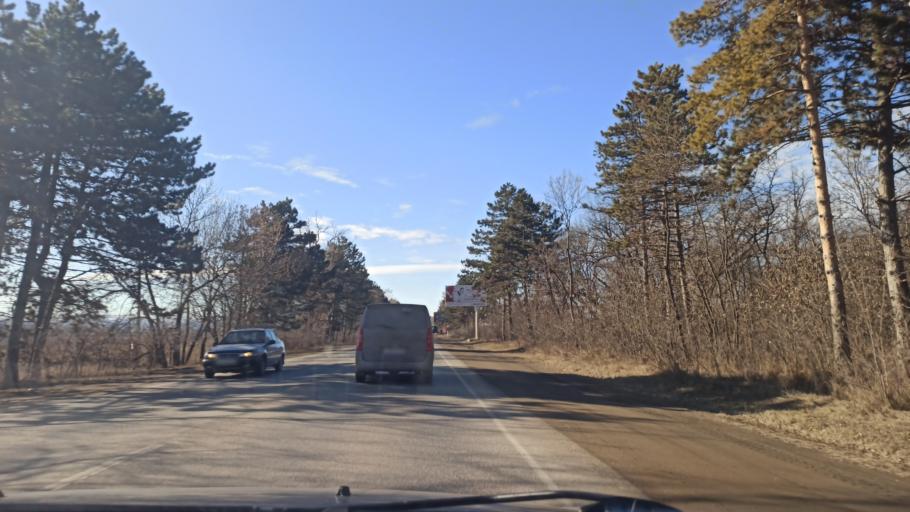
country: RU
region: Stavropol'skiy
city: Vinsady
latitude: 44.0550
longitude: 42.9377
